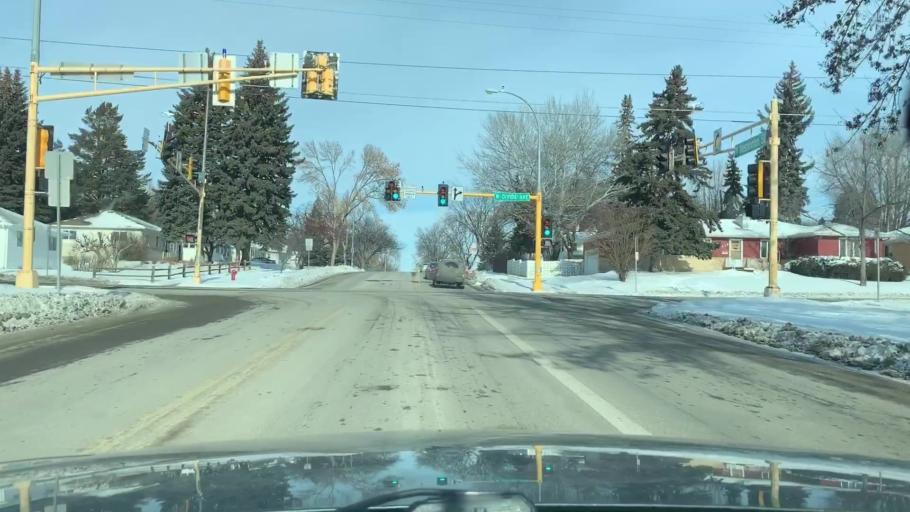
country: US
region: North Dakota
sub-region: Burleigh County
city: Bismarck
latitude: 46.8234
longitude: -100.7941
